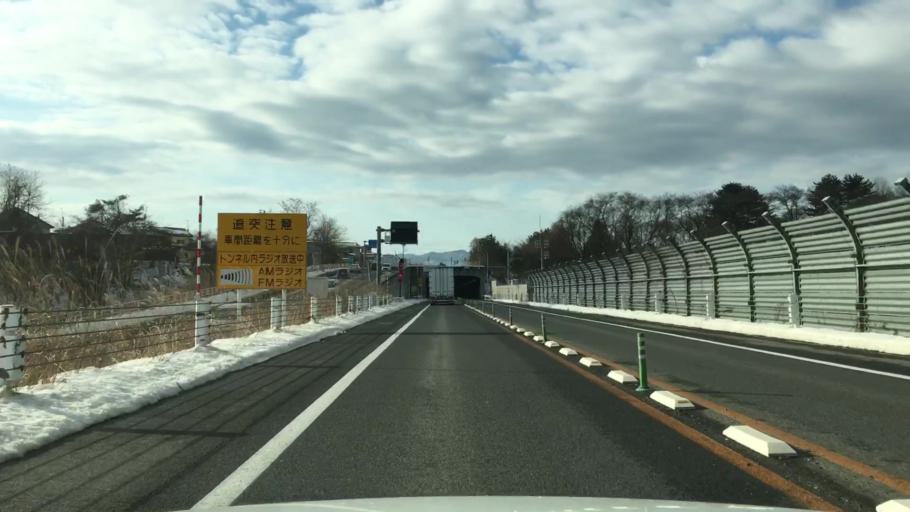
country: JP
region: Akita
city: Odate
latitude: 40.2781
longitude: 140.5364
